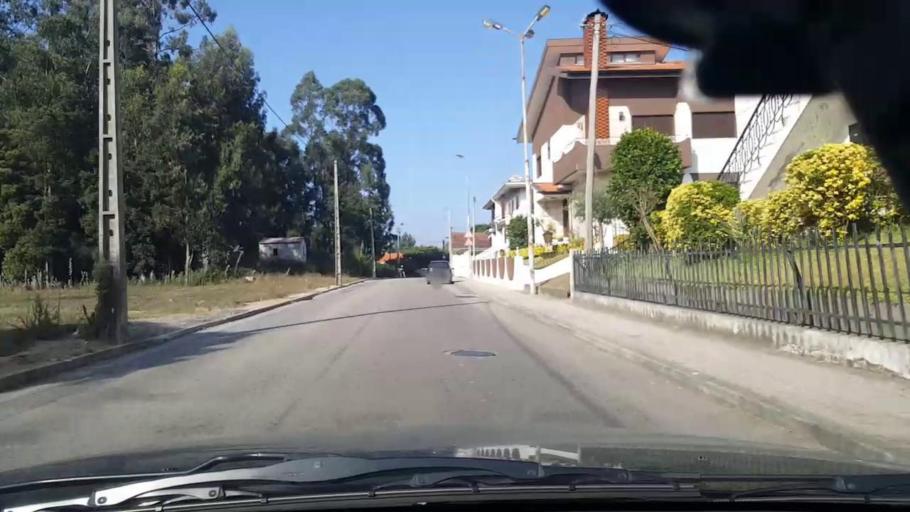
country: PT
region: Porto
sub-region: Maia
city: Gemunde
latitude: 41.2723
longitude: -8.6791
